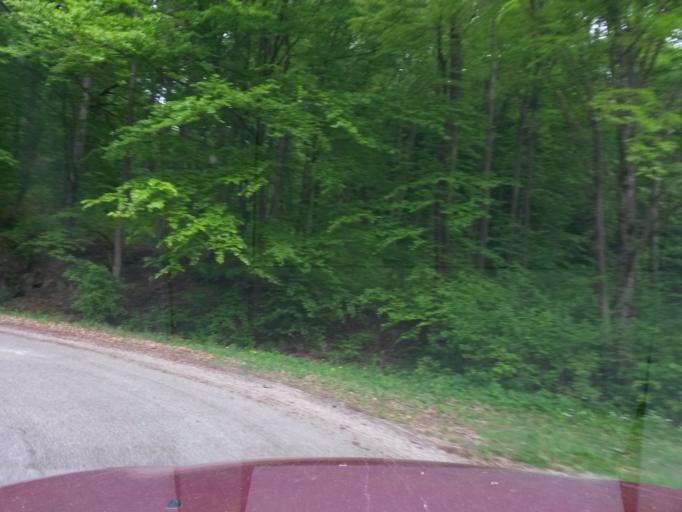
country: SK
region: Kosicky
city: Roznava
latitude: 48.5628
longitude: 20.4703
